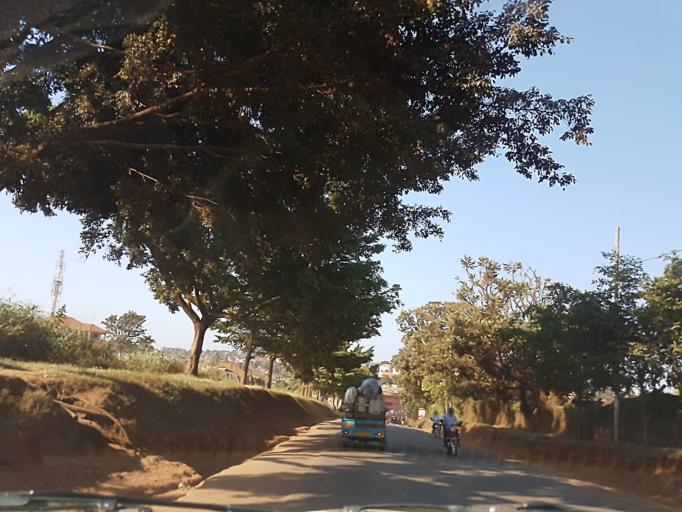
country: UG
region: Central Region
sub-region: Wakiso District
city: Kireka
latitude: 0.3399
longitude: 32.6152
